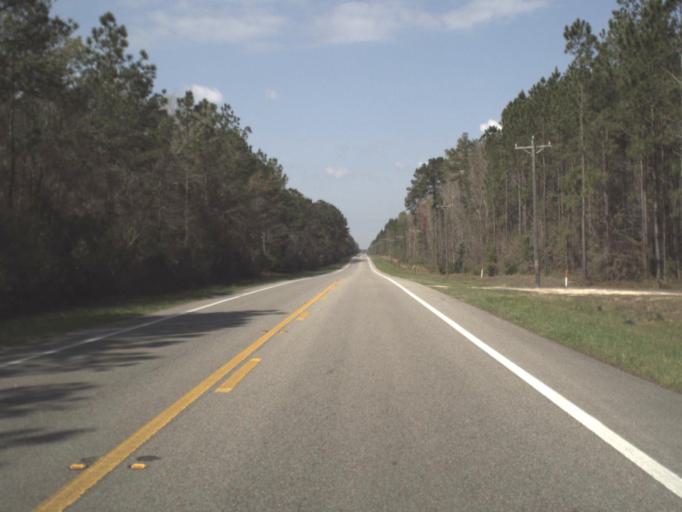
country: US
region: Florida
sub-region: Liberty County
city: Bristol
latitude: 30.3849
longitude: -84.7521
